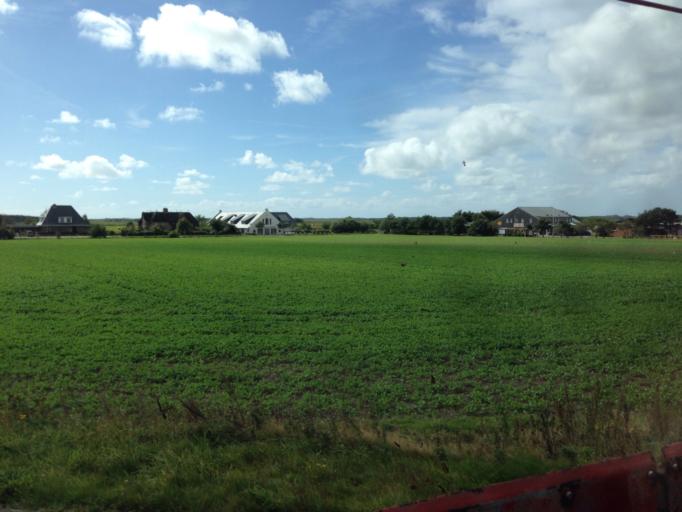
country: DE
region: Schleswig-Holstein
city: Keitum
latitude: 54.8923
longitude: 8.3596
